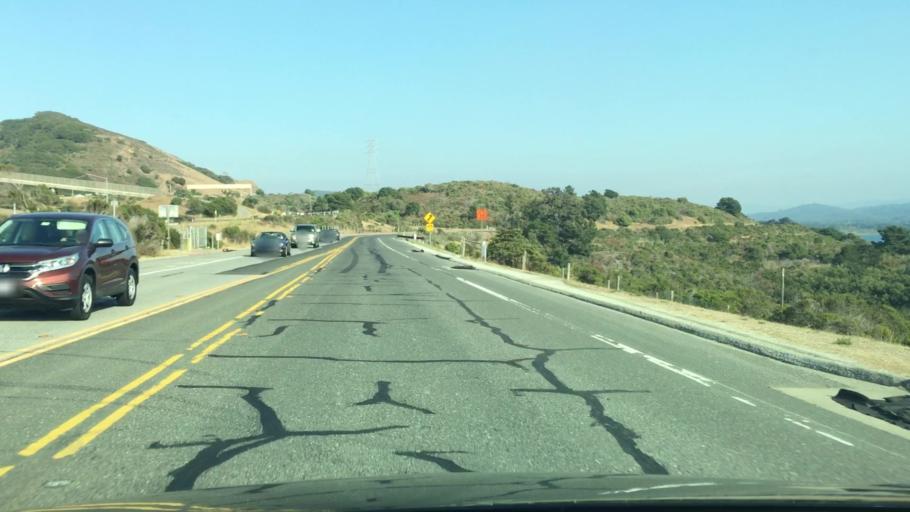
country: US
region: California
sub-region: San Mateo County
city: Highlands-Baywood Park
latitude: 37.5052
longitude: -122.3389
